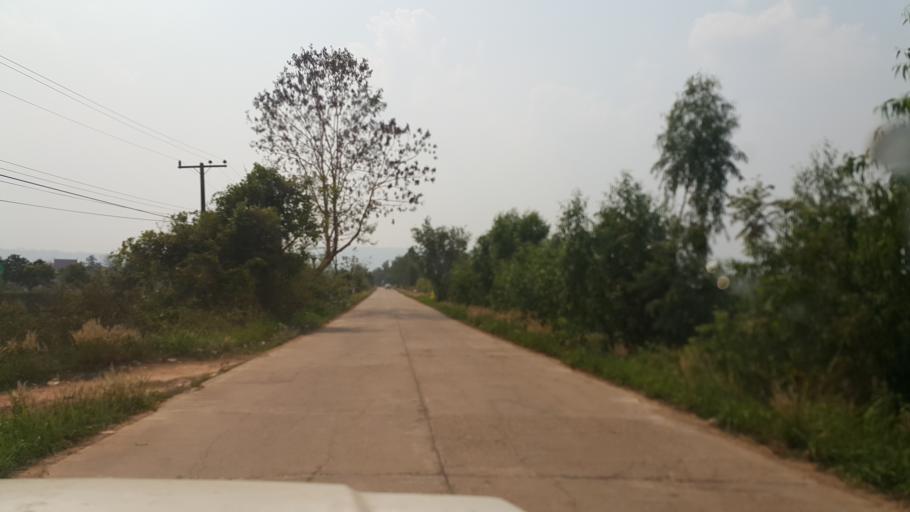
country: TH
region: Nakhon Phanom
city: Ban Phaeng
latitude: 17.9633
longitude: 104.1973
